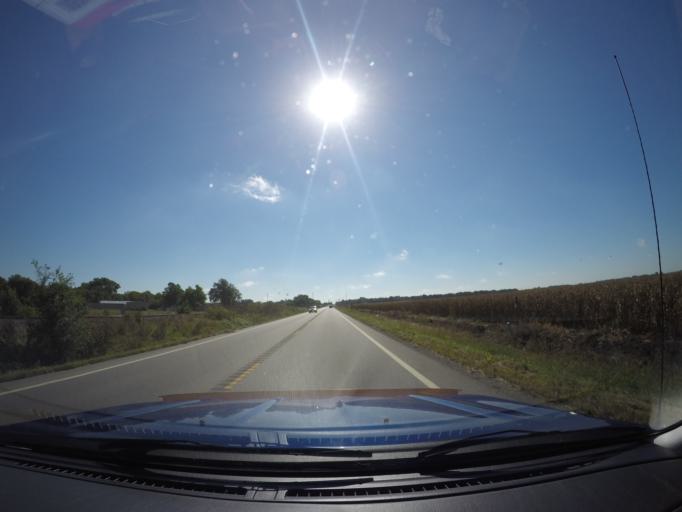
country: US
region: Kansas
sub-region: Shawnee County
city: Rossville
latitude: 39.1431
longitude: -95.9656
